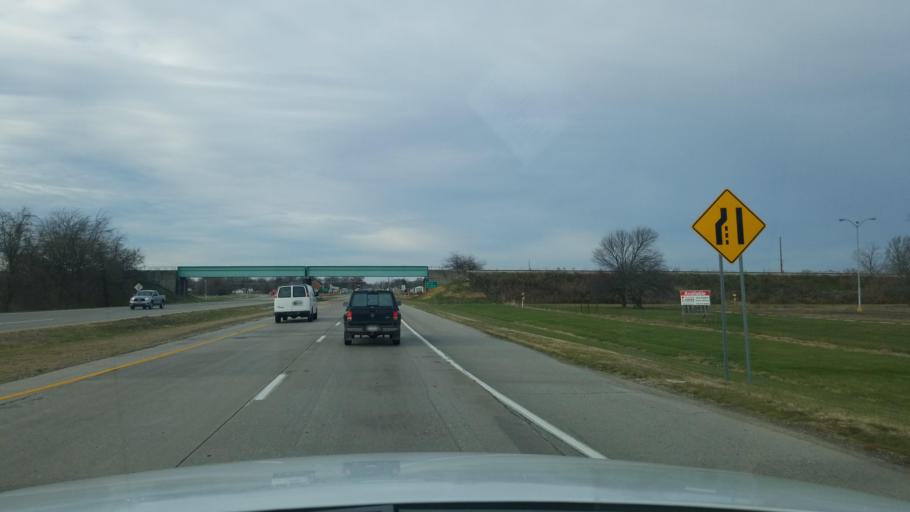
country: US
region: Indiana
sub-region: Posey County
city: Mount Vernon
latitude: 37.9387
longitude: -87.8705
